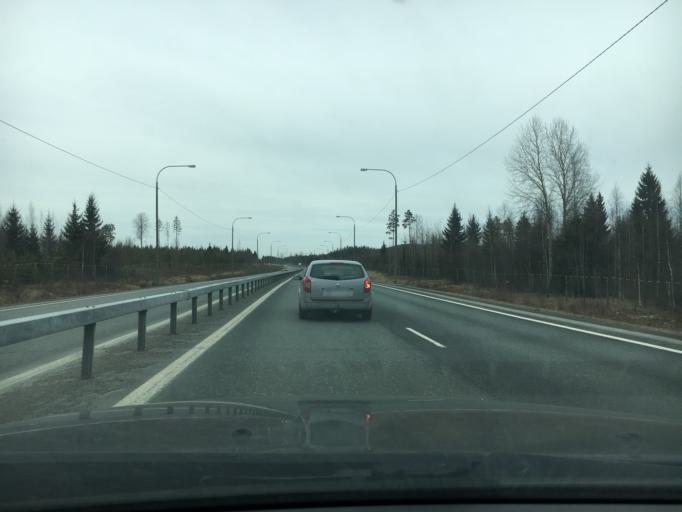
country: FI
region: Northern Savo
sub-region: Kuopio
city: Kuopio
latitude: 62.7731
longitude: 27.5866
